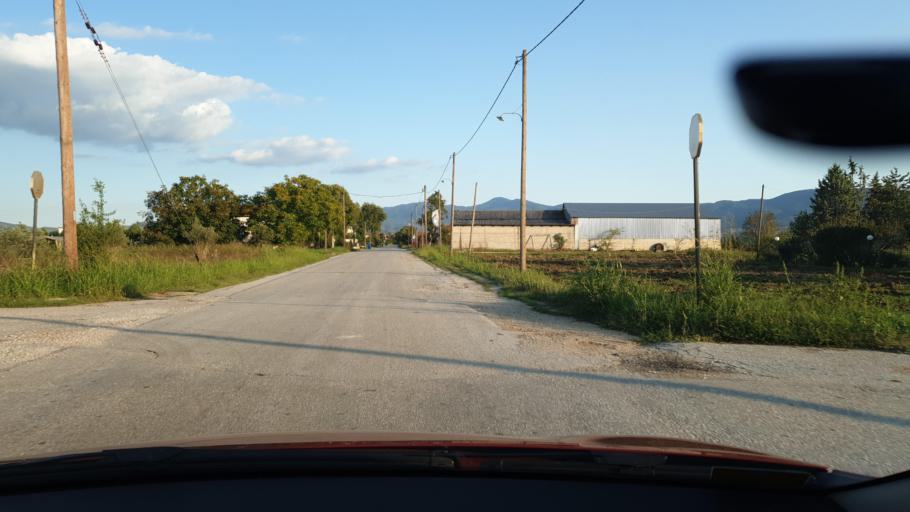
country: GR
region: Central Macedonia
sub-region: Nomos Thessalonikis
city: Nea Apollonia
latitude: 40.5507
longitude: 23.4443
